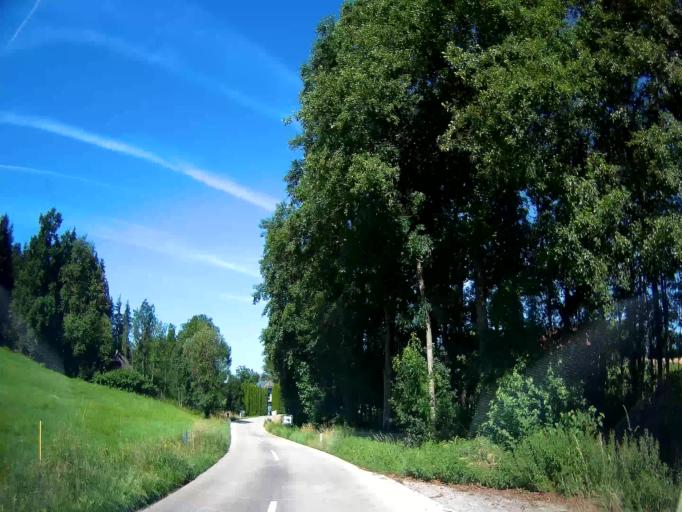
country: AT
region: Carinthia
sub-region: Politischer Bezirk Klagenfurt Land
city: Maria Saal
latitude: 46.6939
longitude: 14.3759
